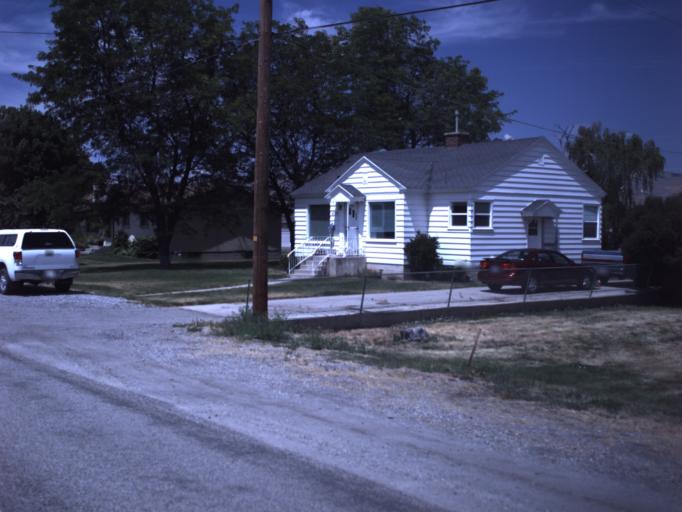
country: US
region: Utah
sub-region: Box Elder County
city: Tremonton
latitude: 41.7121
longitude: -112.1560
